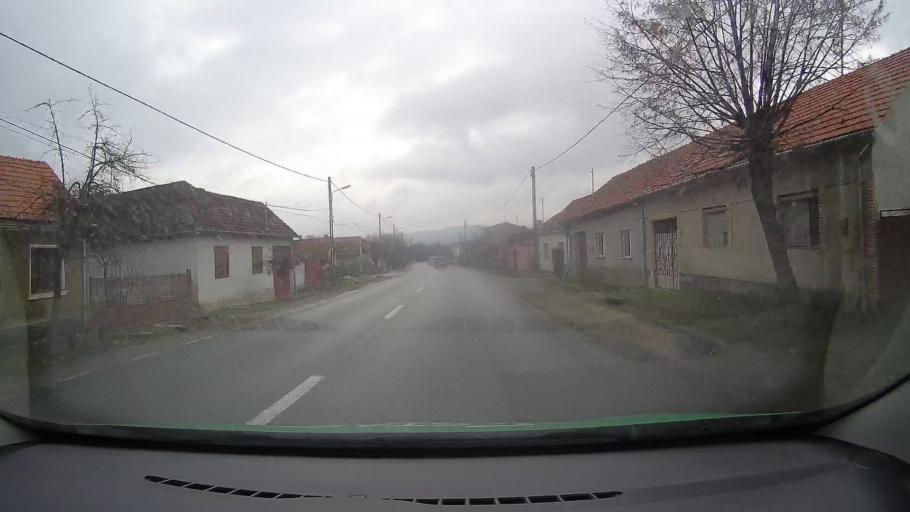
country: RO
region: Hunedoara
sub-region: Comuna Dobra
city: Dobra
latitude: 45.9180
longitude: 22.5587
